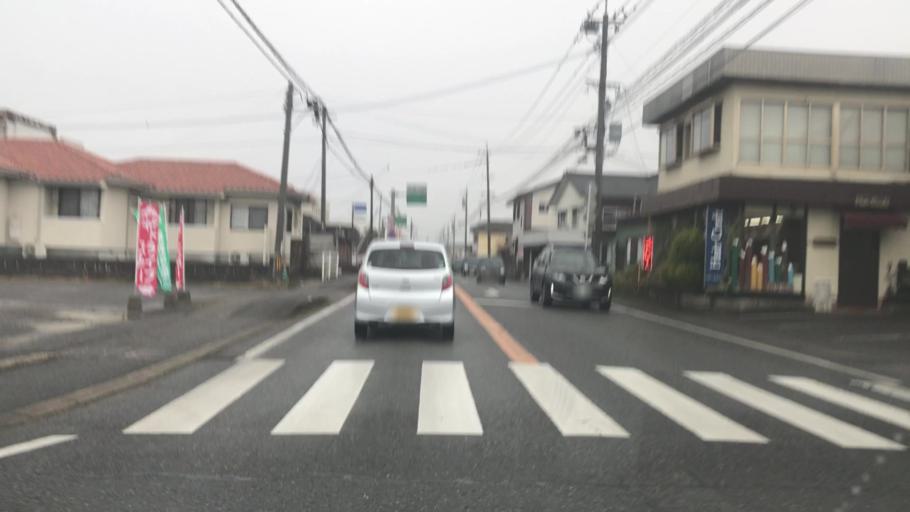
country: JP
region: Saga Prefecture
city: Takeocho-takeo
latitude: 33.2072
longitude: 130.0400
